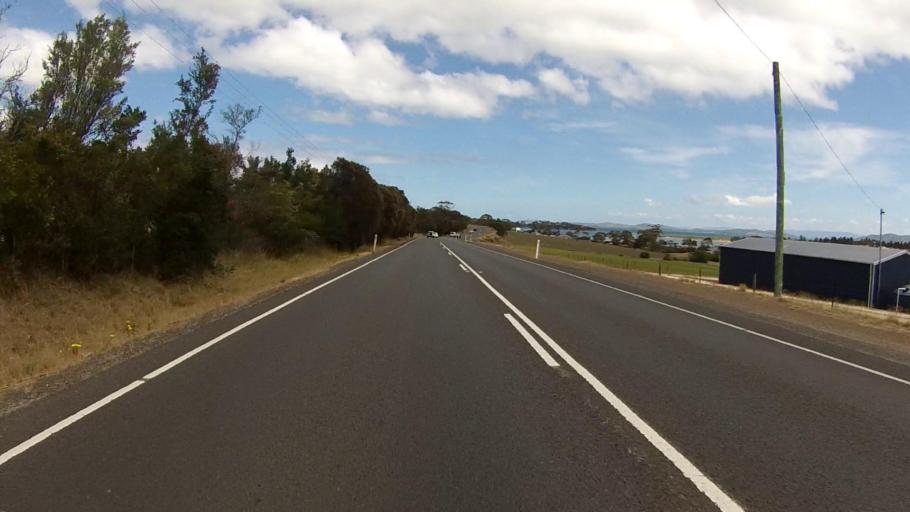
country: AU
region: Tasmania
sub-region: Sorell
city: Sorell
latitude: -42.8350
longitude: 147.6243
